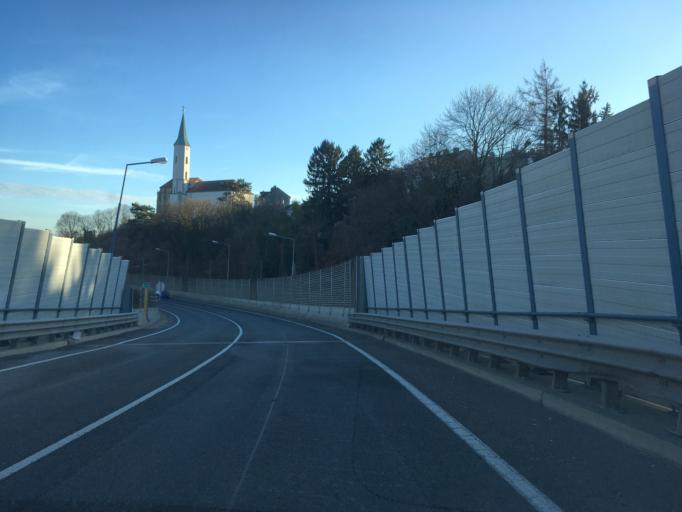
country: AT
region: Lower Austria
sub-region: Politischer Bezirk Wien-Umgebung
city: Klosterneuburg
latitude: 48.3164
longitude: 16.3167
